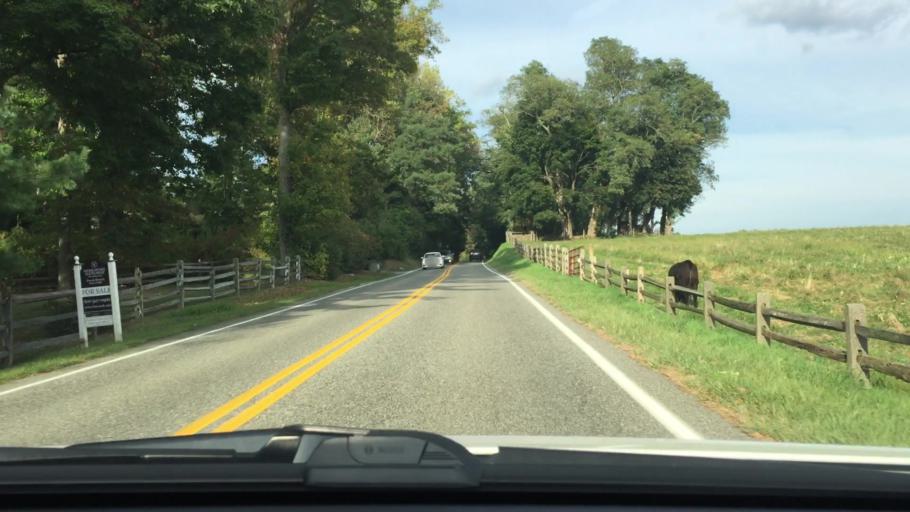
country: US
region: Pennsylvania
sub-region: Delaware County
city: Wayne
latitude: 40.0209
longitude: -75.3884
